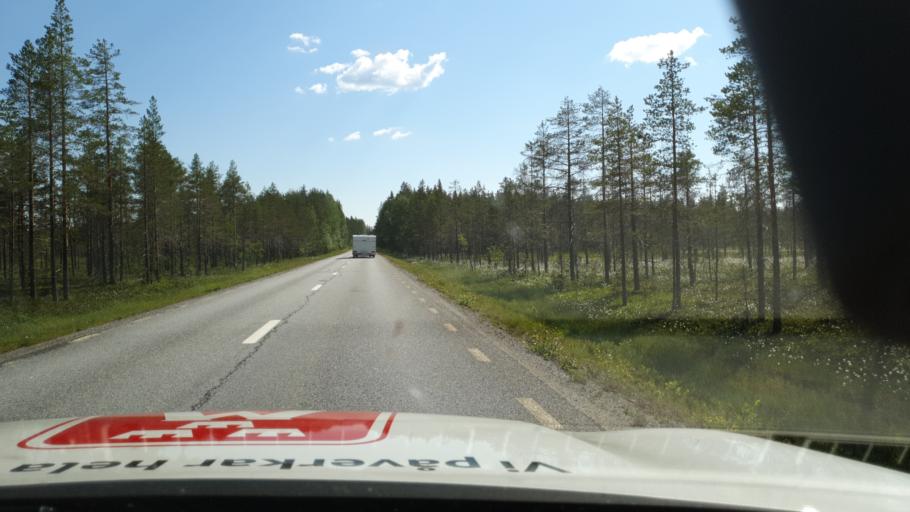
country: SE
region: Vaesterbotten
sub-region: Skelleftea Kommun
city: Burtraesk
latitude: 64.3587
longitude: 20.2437
